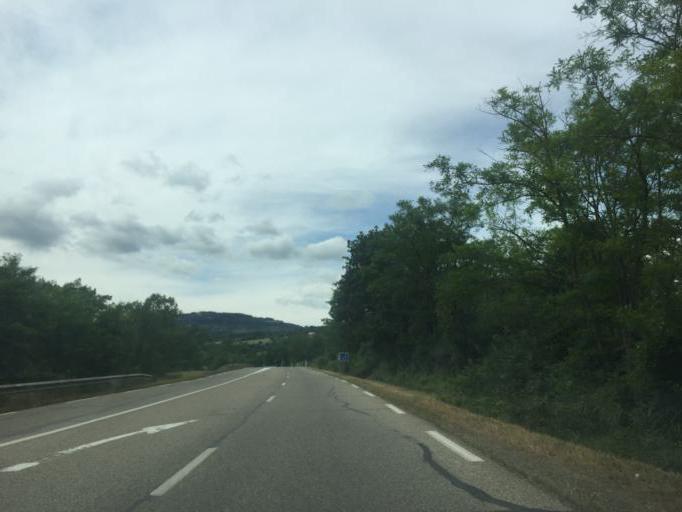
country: FR
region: Rhone-Alpes
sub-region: Departement de l'Ardeche
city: Alba-la-Romaine
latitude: 44.5877
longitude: 4.5577
